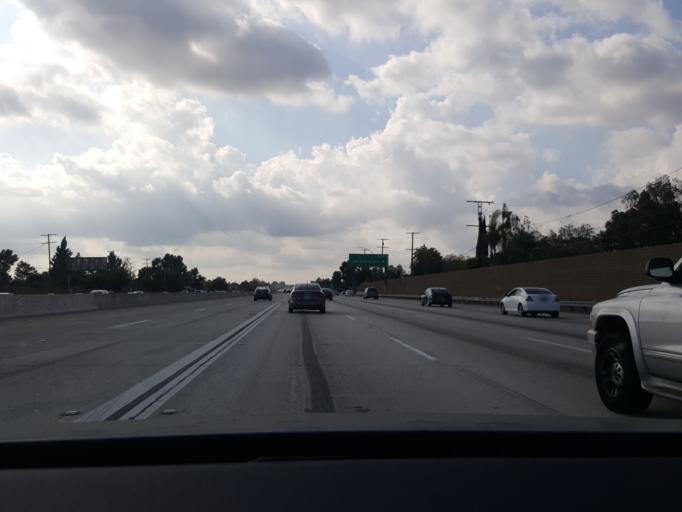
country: US
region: California
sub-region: Los Angeles County
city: South San Gabriel
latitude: 34.0722
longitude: -118.0863
